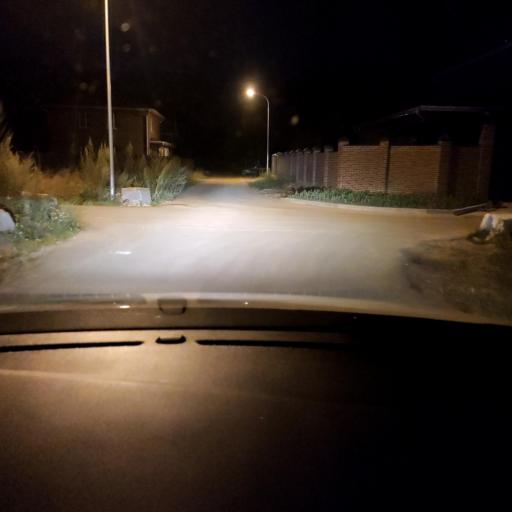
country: RU
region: Tatarstan
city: Osinovo
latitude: 55.8601
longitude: 48.7900
